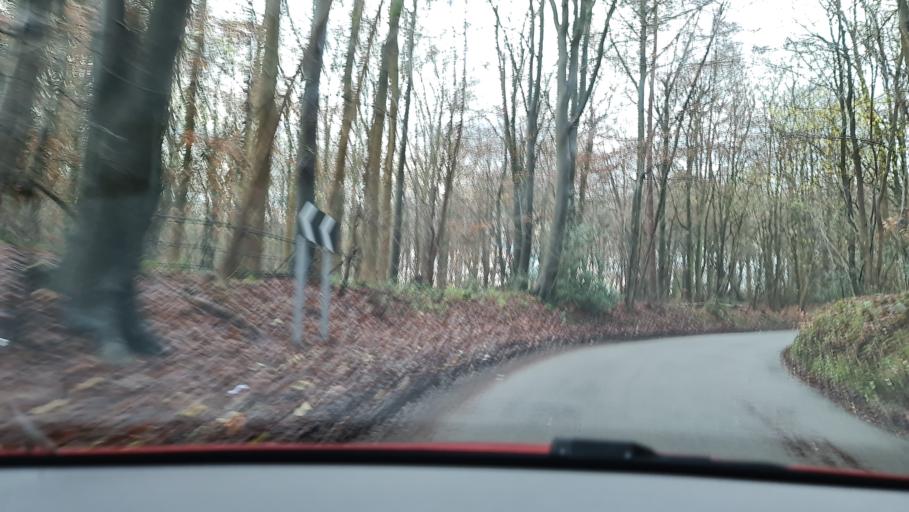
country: GB
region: England
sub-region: Buckinghamshire
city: Little Chalfont
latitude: 51.6764
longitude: -0.5641
